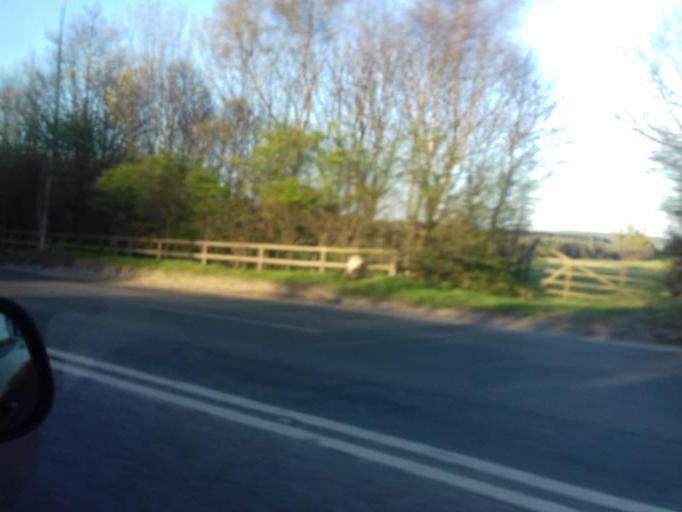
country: IE
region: Leinster
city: Lusk
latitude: 53.4970
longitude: -6.1940
